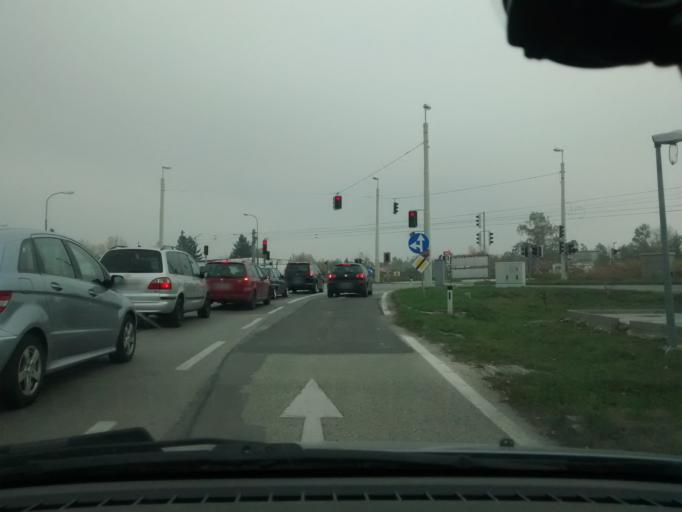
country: AT
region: Lower Austria
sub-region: Politischer Bezirk Modling
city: Guntramsdorf
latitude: 48.0360
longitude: 16.3022
